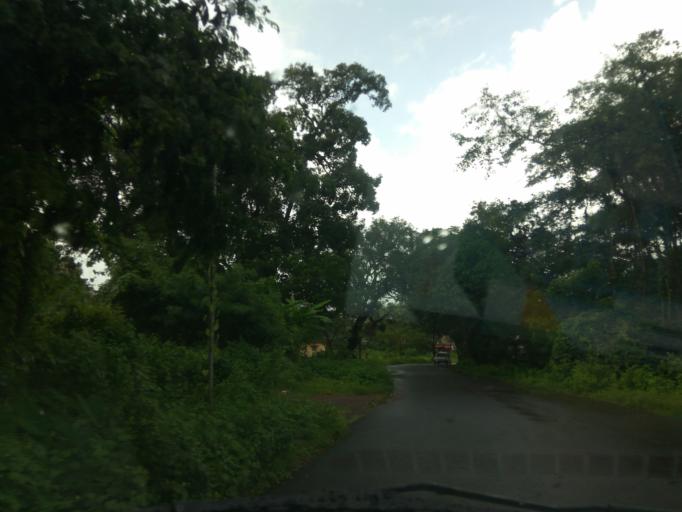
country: IN
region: Goa
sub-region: North Goa
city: Goa Velha
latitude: 15.4422
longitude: 73.8645
